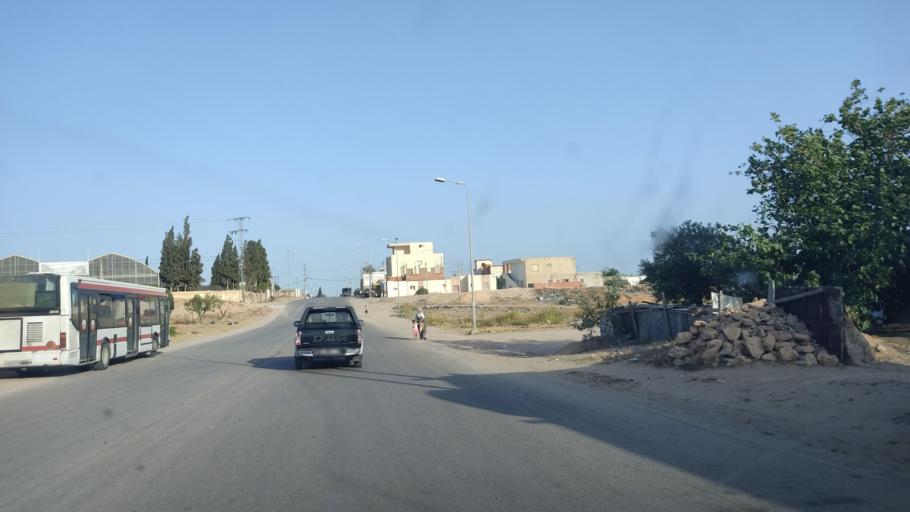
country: TN
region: Safaqis
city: Sfax
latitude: 34.7951
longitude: 10.6818
